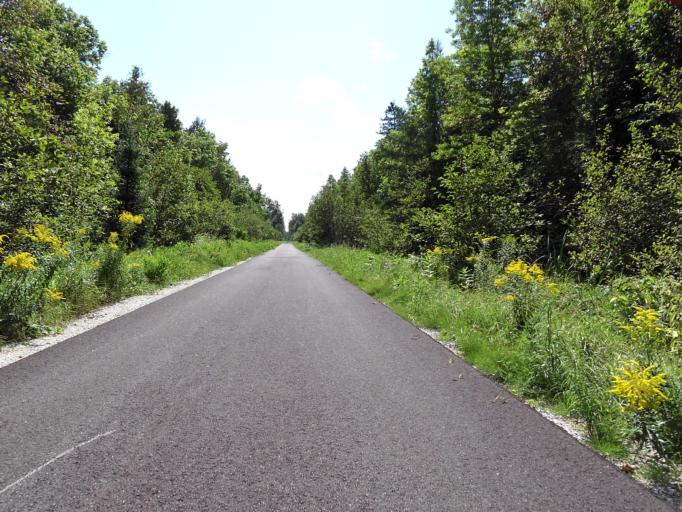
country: CA
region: Quebec
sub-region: Outaouais
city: Maniwaki
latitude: 46.1829
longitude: -76.0435
